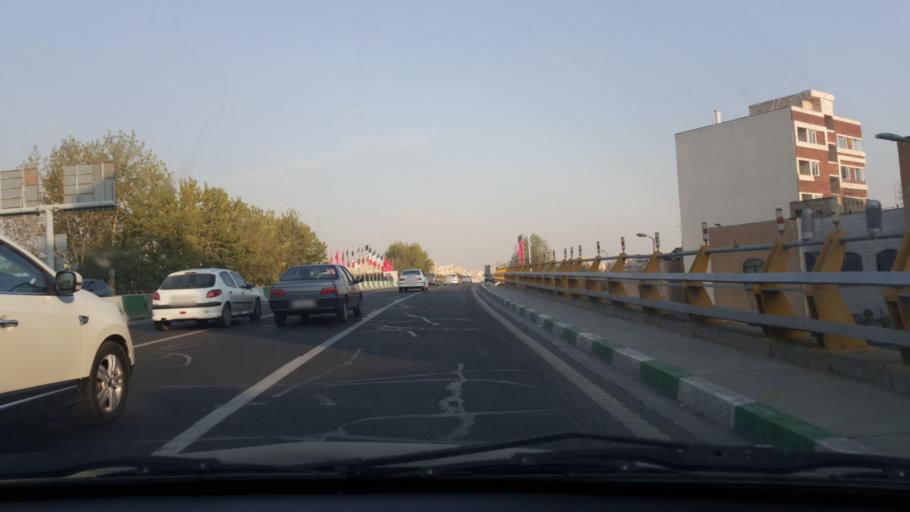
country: IR
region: Tehran
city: Tehran
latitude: 35.7335
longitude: 51.2932
